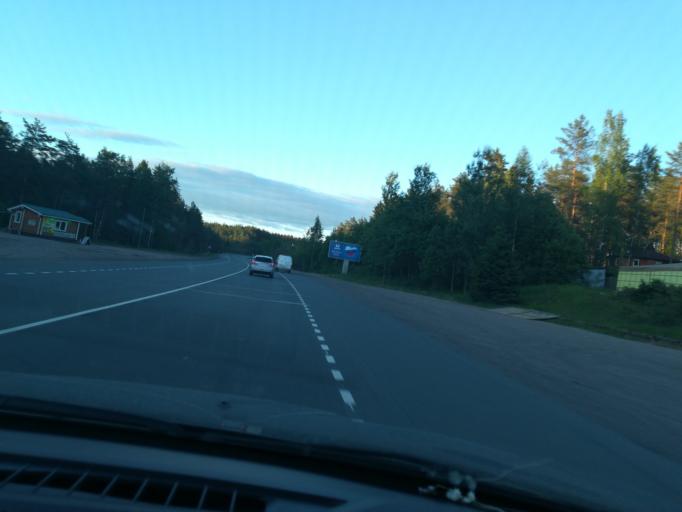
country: RU
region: Leningrad
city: Yakovlevo
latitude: 60.3606
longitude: 29.5462
